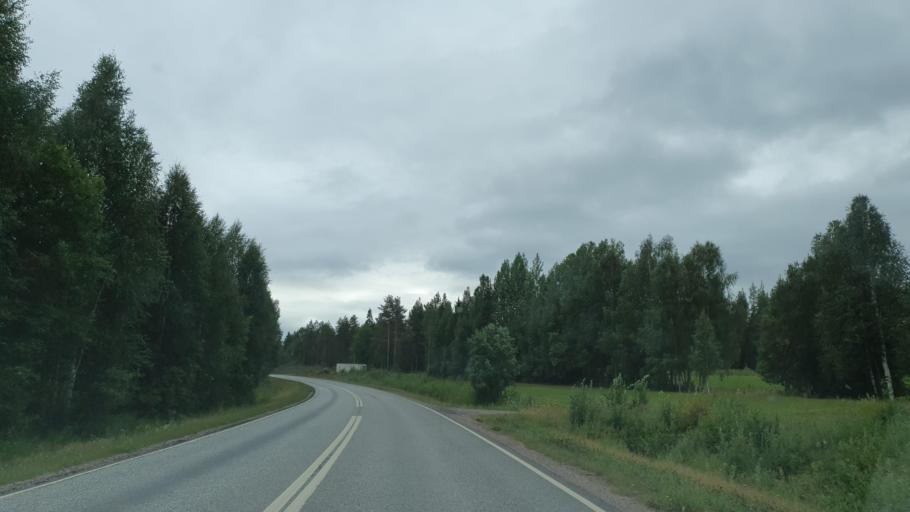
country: FI
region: Lapland
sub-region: Rovaniemi
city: Rovaniemi
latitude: 66.7414
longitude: 25.4376
